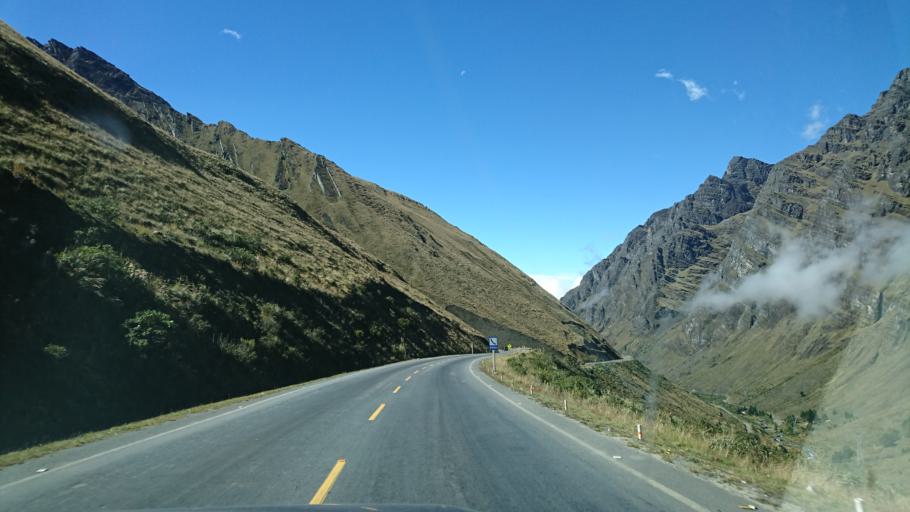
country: BO
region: La Paz
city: La Paz
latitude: -16.3297
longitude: -67.9594
